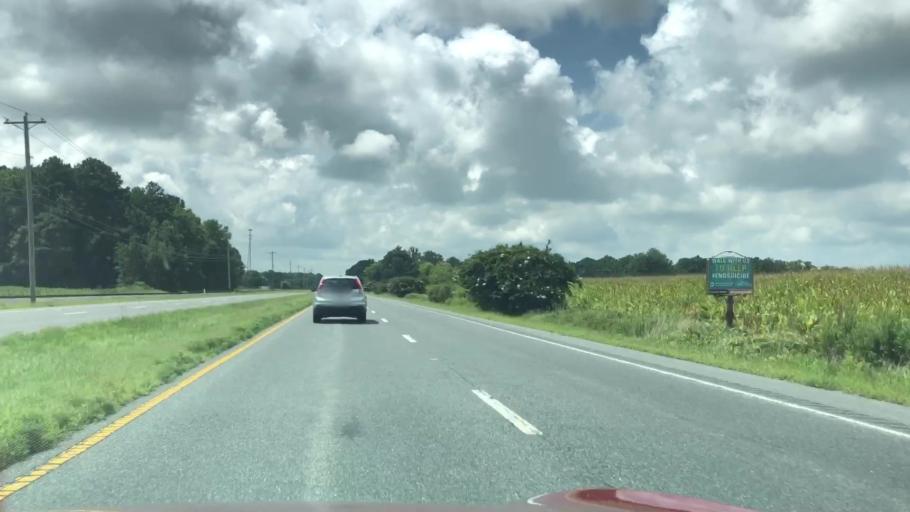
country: US
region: Virginia
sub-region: Northampton County
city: Exmore
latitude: 37.4420
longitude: -75.8790
